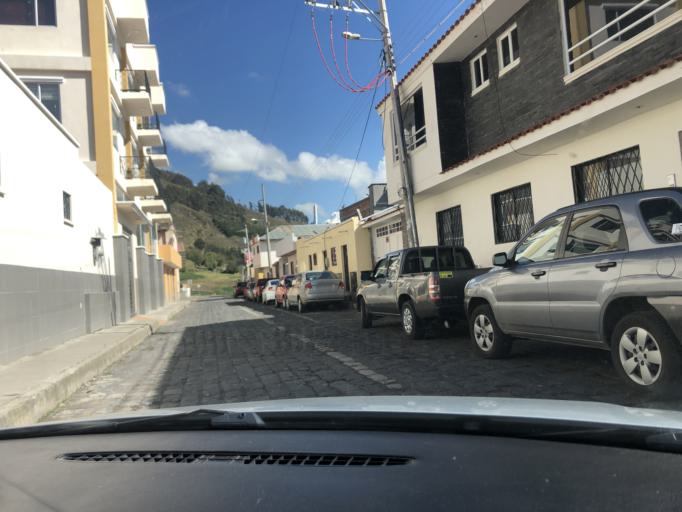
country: EC
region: Chimborazo
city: Riobamba
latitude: -1.7015
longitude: -78.7724
